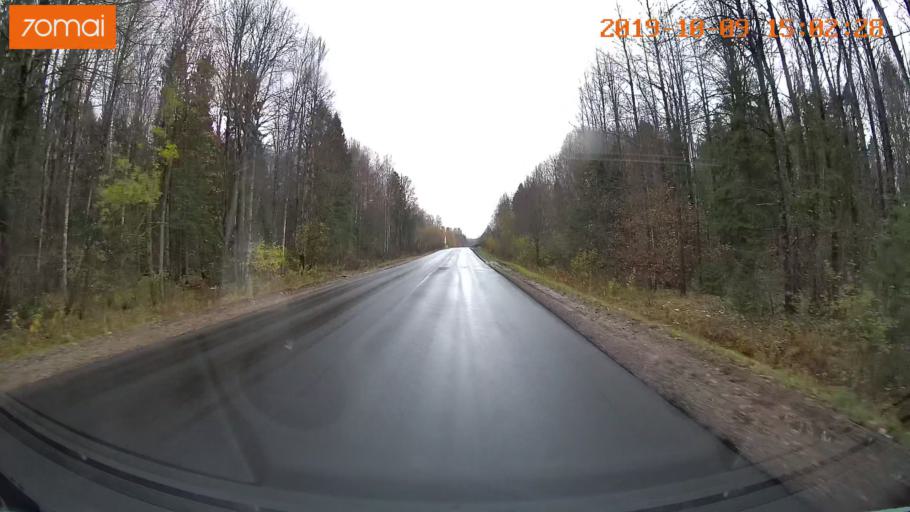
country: RU
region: Kostroma
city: Chistyye Bory
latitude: 58.2847
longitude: 41.6789
